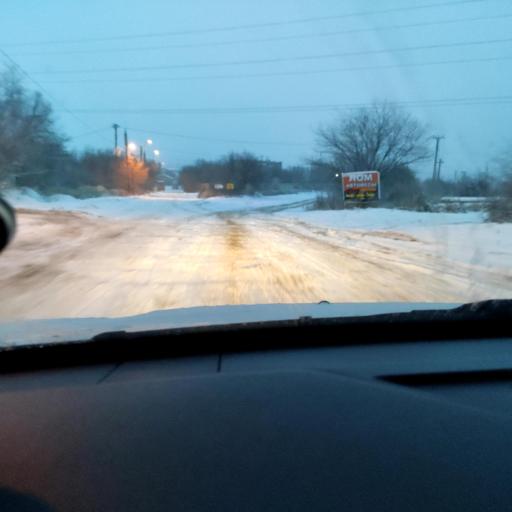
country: RU
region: Samara
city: Smyshlyayevka
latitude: 53.2399
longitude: 50.4806
